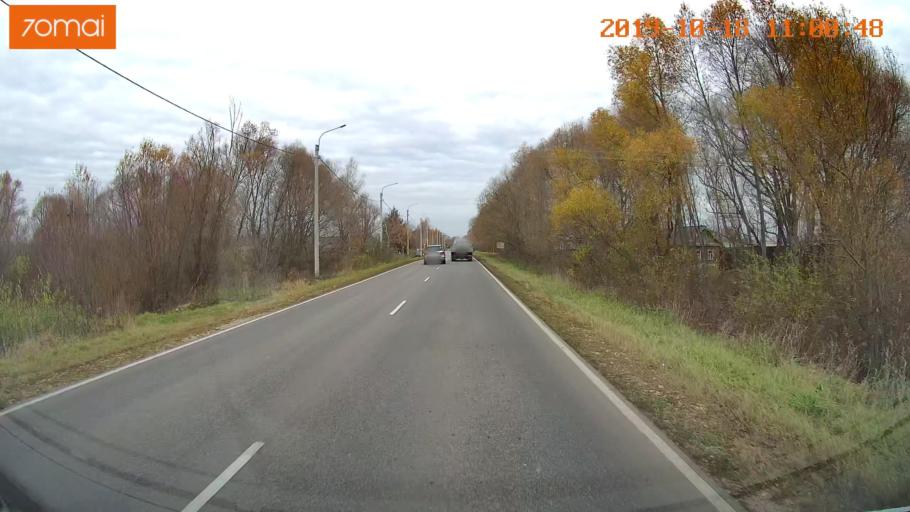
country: RU
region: Tula
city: Yepifan'
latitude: 53.8473
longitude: 38.5528
